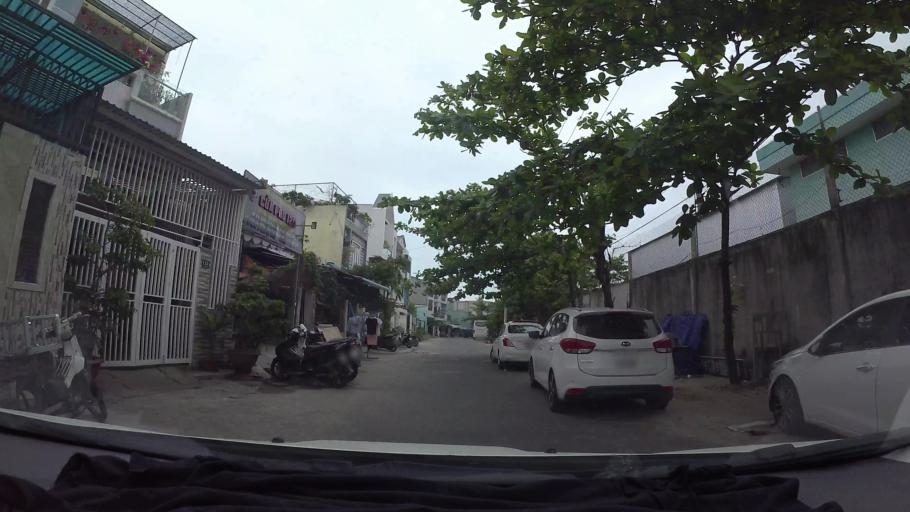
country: VN
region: Da Nang
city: Thanh Khe
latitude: 16.0675
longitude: 108.1778
